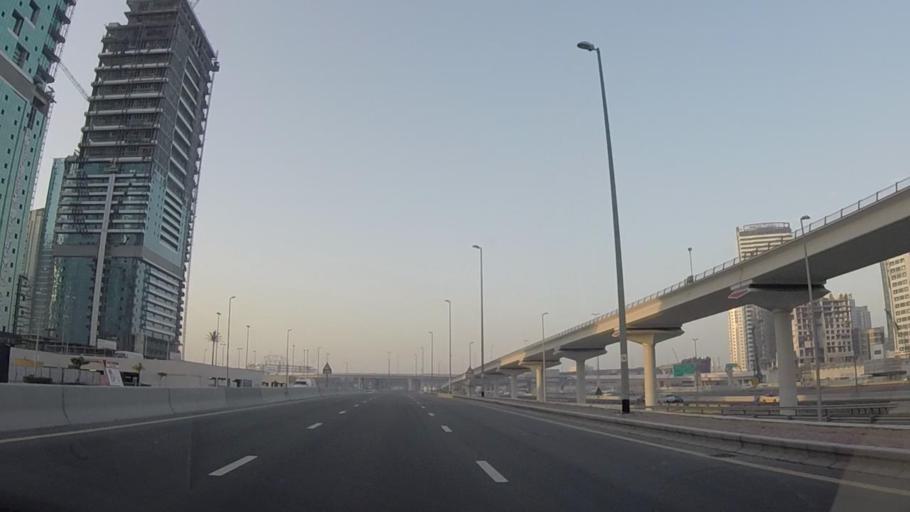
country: AE
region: Dubai
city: Dubai
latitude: 25.0695
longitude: 55.1380
